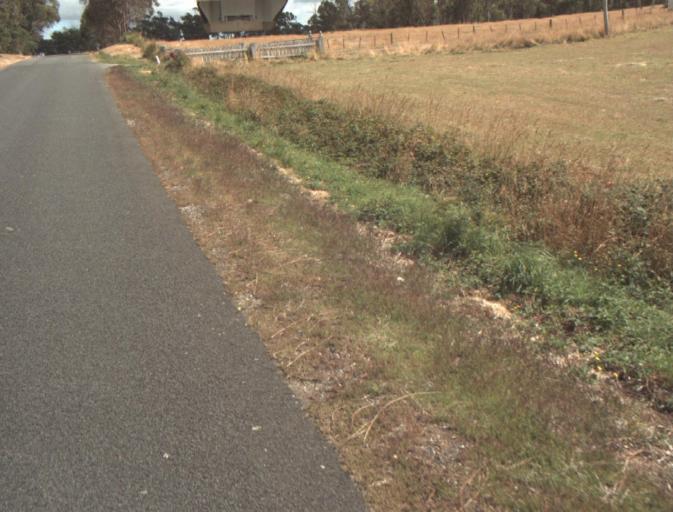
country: AU
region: Tasmania
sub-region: Launceston
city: Mayfield
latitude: -41.2053
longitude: 147.0959
